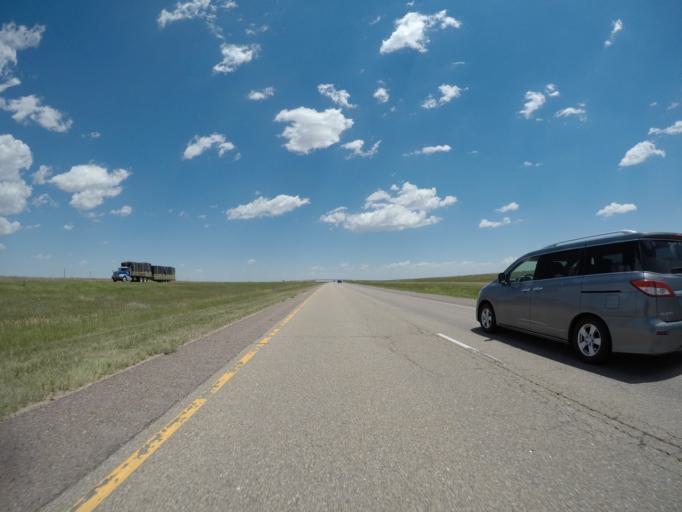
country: US
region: Colorado
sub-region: Lincoln County
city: Hugo
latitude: 39.2805
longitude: -103.3566
